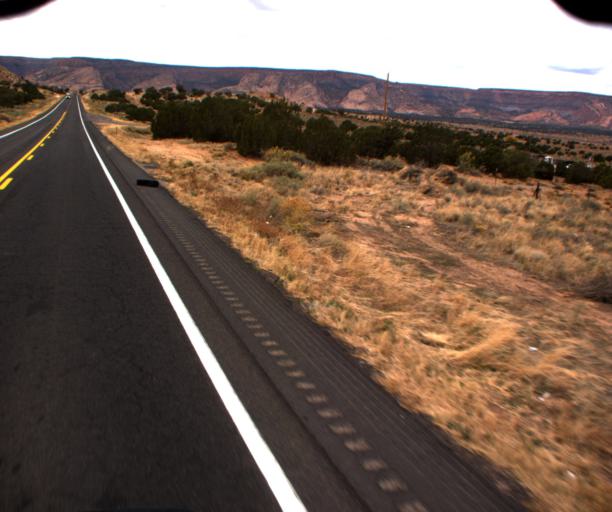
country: US
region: Arizona
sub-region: Navajo County
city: Kayenta
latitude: 36.6968
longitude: -110.3455
